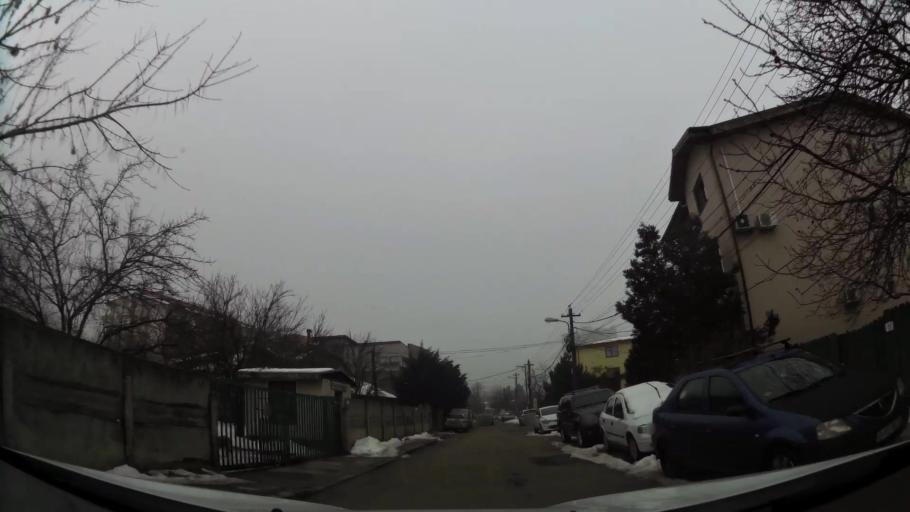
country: RO
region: Ilfov
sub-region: Comuna Chiajna
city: Rosu
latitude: 44.4458
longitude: 26.0247
